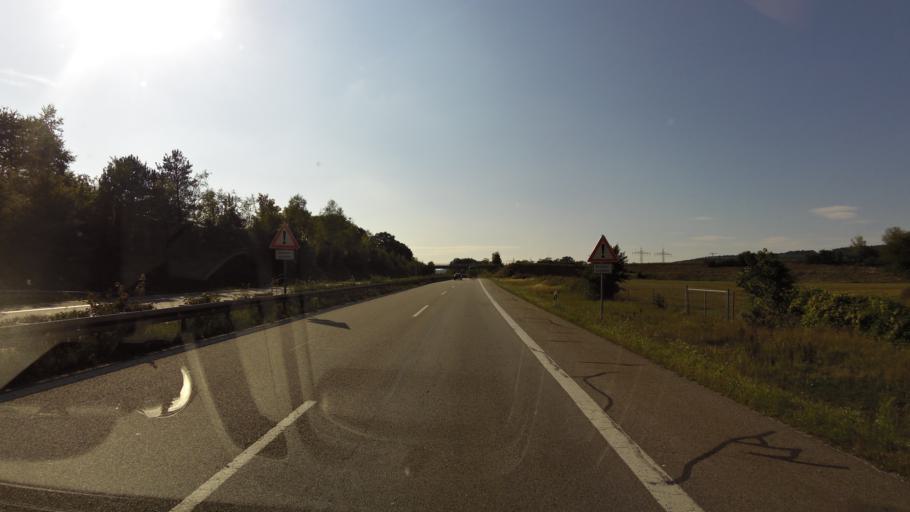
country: DE
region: Bavaria
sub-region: Upper Bavaria
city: Marktl
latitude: 48.2491
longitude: 12.8050
